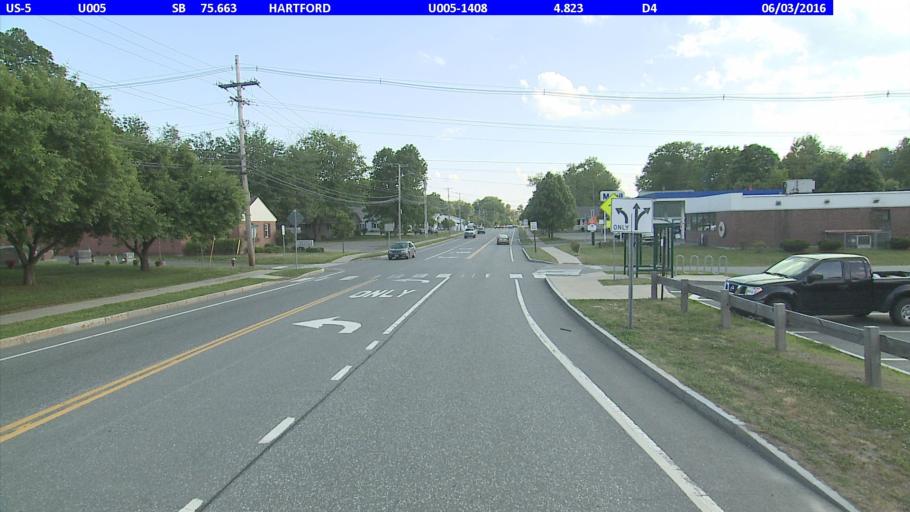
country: US
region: Vermont
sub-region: Windsor County
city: Wilder
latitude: 43.6617
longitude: -72.3138
